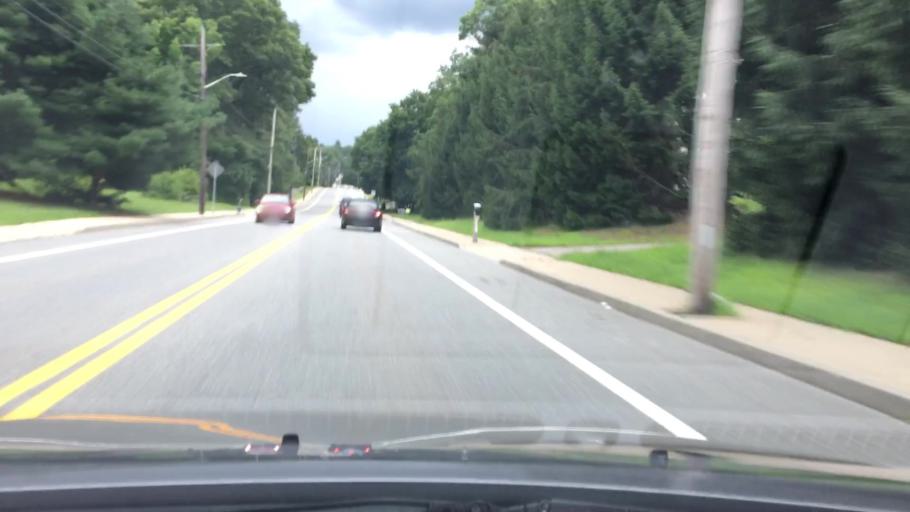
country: US
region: Rhode Island
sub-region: Providence County
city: Cumberland
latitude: 41.9775
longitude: -71.3909
